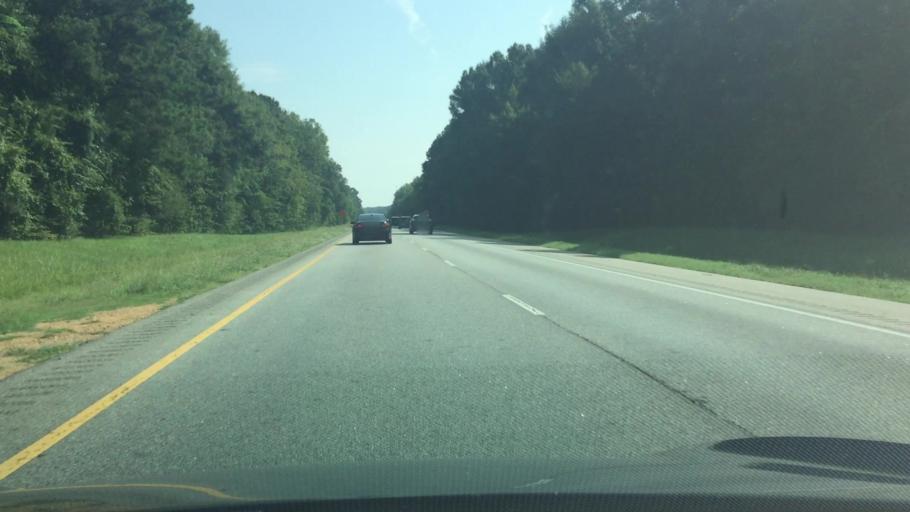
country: US
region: Alabama
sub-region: Montgomery County
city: Montgomery
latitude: 32.2178
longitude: -86.3992
